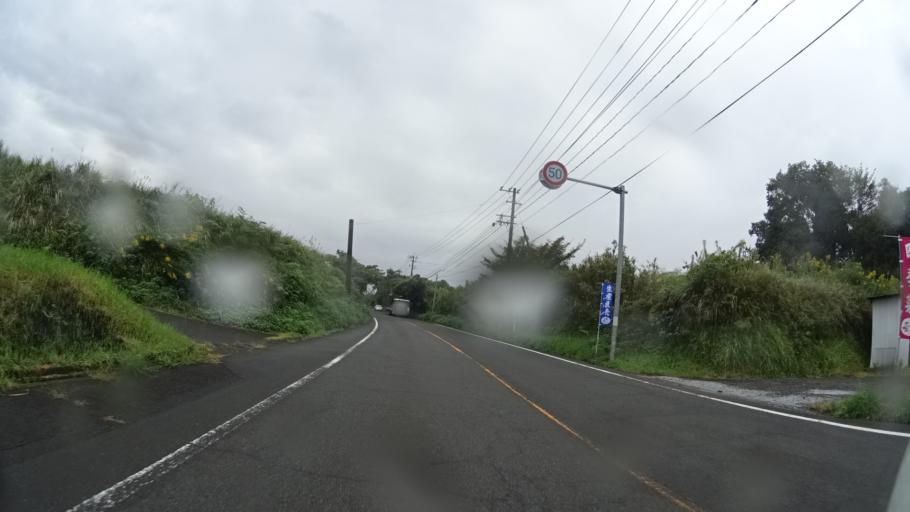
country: JP
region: Kagoshima
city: Kajiki
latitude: 31.7952
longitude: 130.6724
